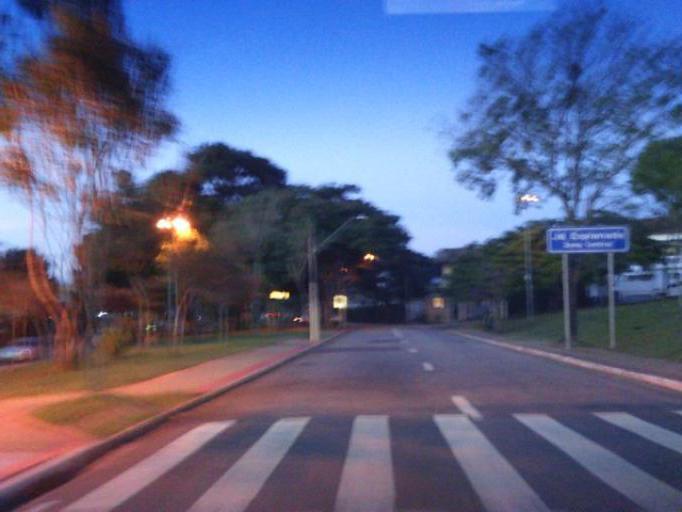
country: BR
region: Sao Paulo
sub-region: Sao Jose Dos Campos
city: Sao Jose dos Campos
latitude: -23.1957
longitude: -45.9080
